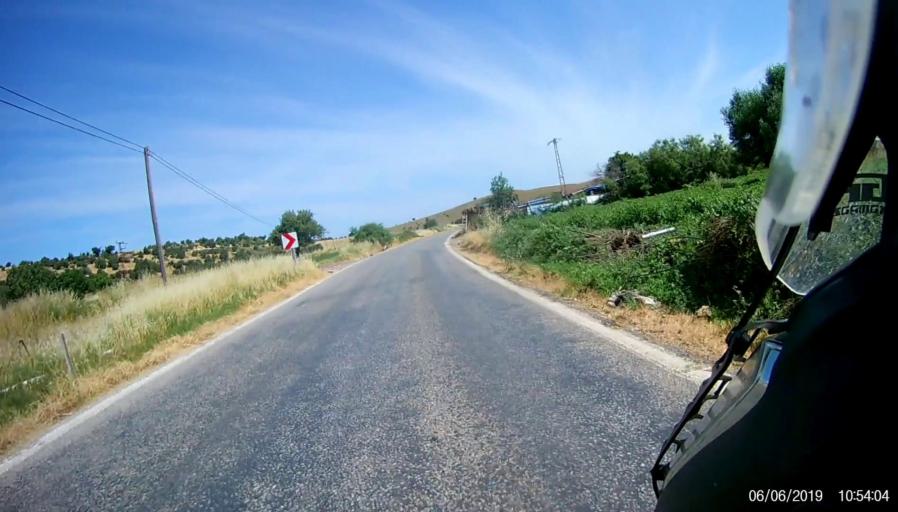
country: TR
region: Canakkale
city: Behram
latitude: 39.5059
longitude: 26.4154
